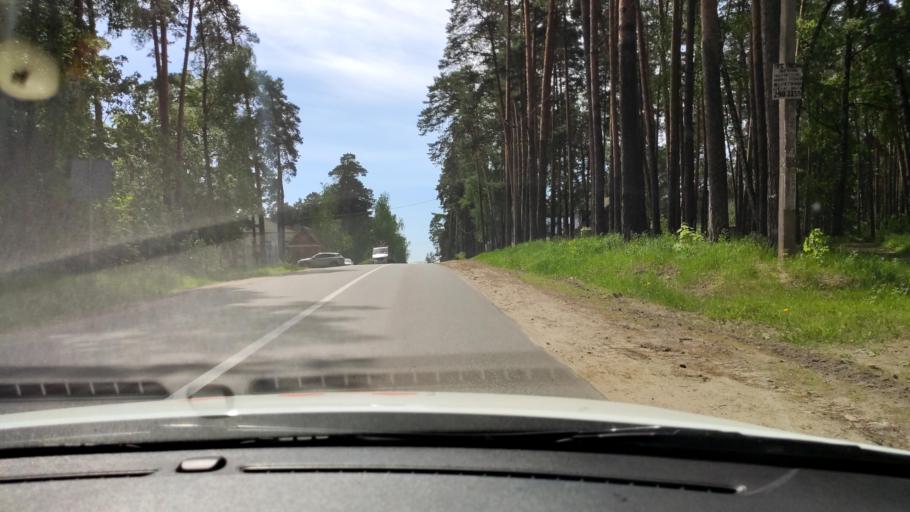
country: RU
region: Tatarstan
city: Osinovo
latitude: 55.8342
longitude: 48.8138
